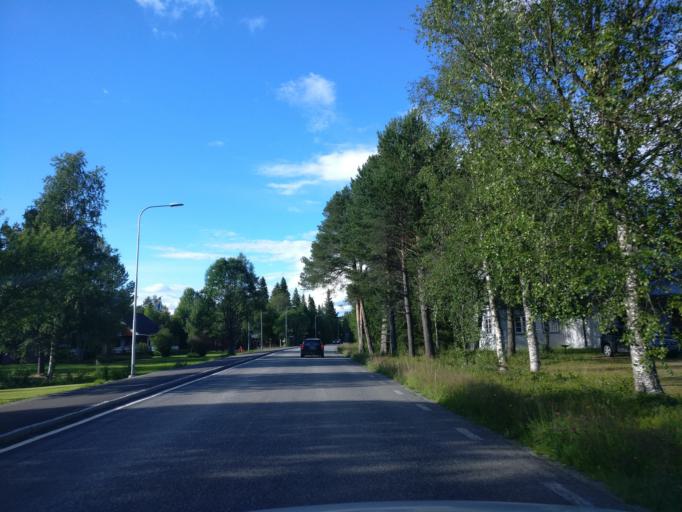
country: SE
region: Jaemtland
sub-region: Harjedalens Kommun
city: Sveg
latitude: 62.4589
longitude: 13.8645
